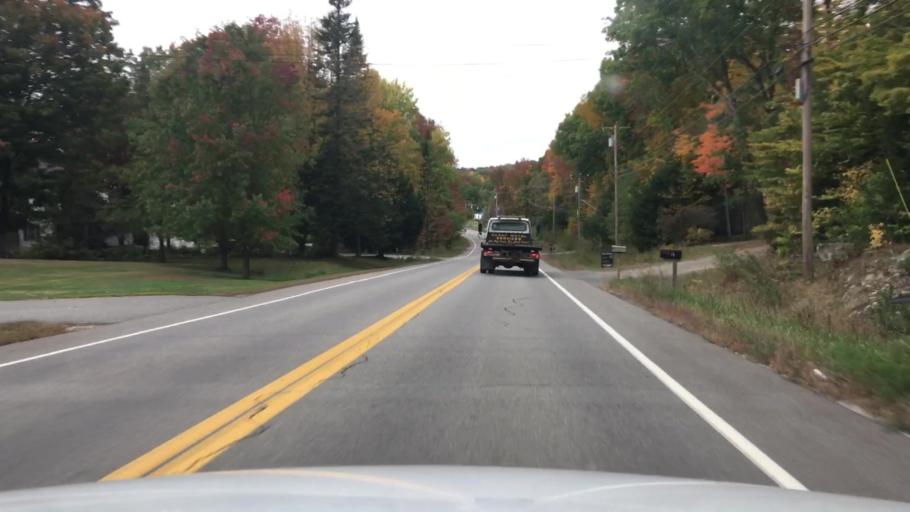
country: US
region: Maine
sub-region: Kennebec County
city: Oakland
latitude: 44.5609
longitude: -69.7447
